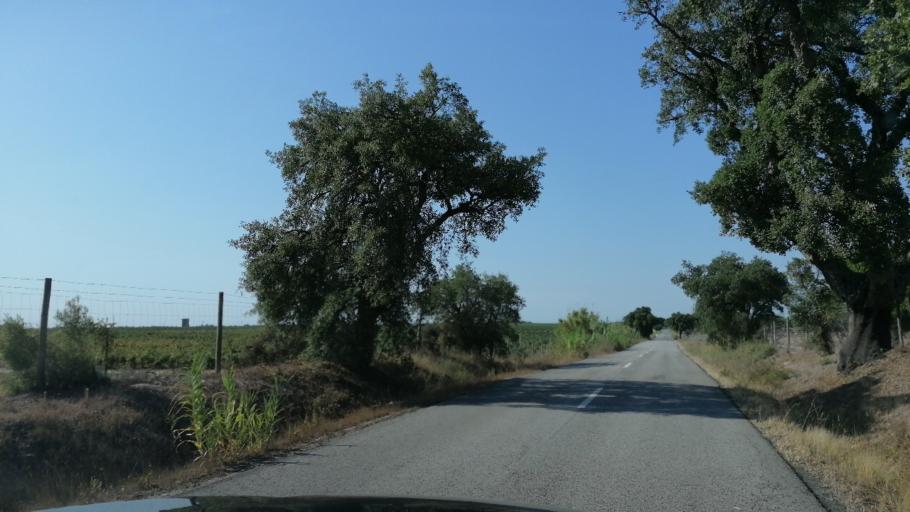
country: PT
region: Evora
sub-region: Vendas Novas
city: Vendas Novas
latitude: 38.7322
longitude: -8.6239
